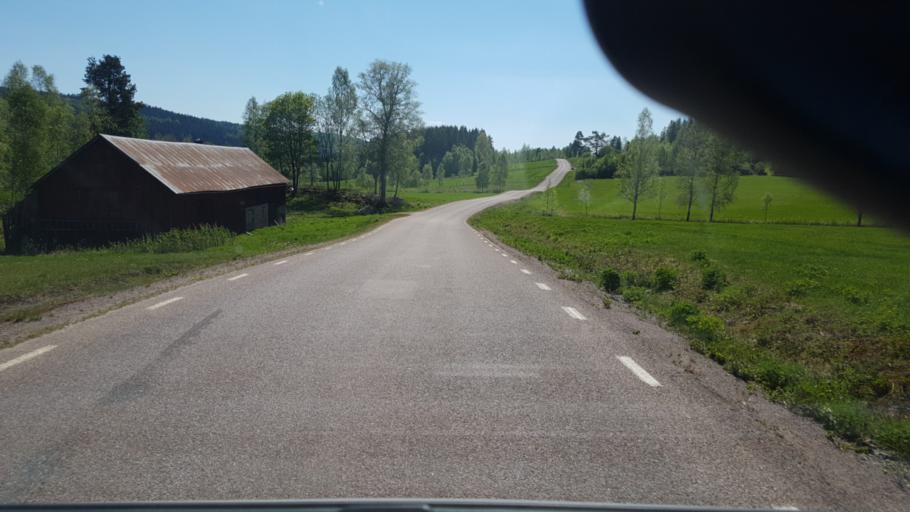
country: SE
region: Vaermland
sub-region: Arvika Kommun
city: Arvika
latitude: 59.7714
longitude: 12.8204
